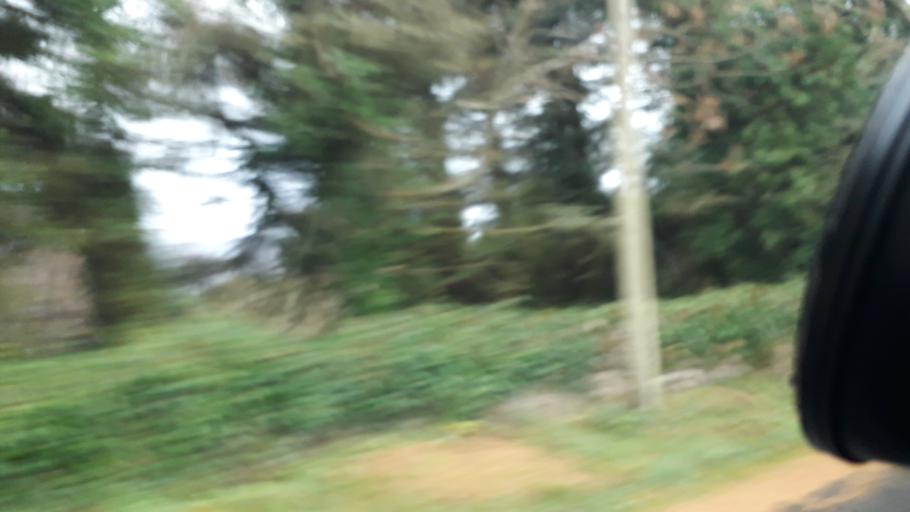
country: IE
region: Ulster
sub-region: County Donegal
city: Buncrana
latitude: 55.2215
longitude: -7.6111
